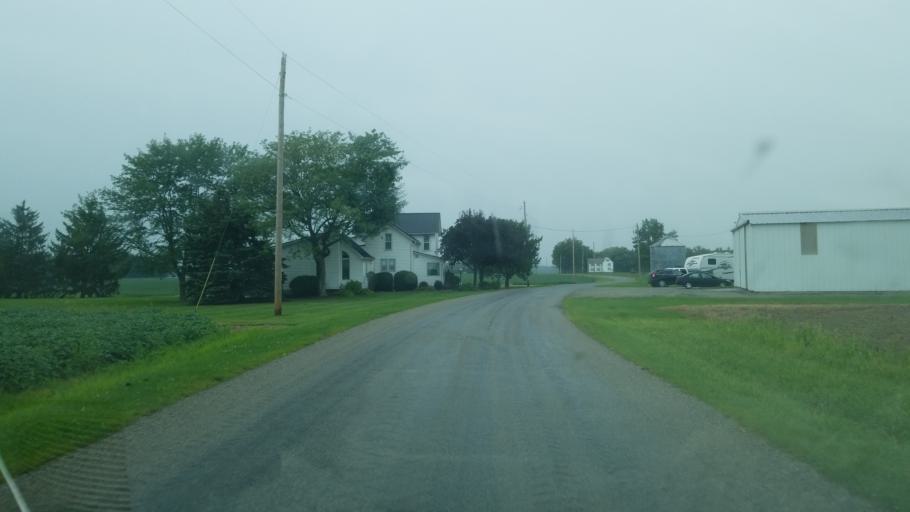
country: US
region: Ohio
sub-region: Huron County
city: Willard
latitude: 41.0164
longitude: -82.8130
